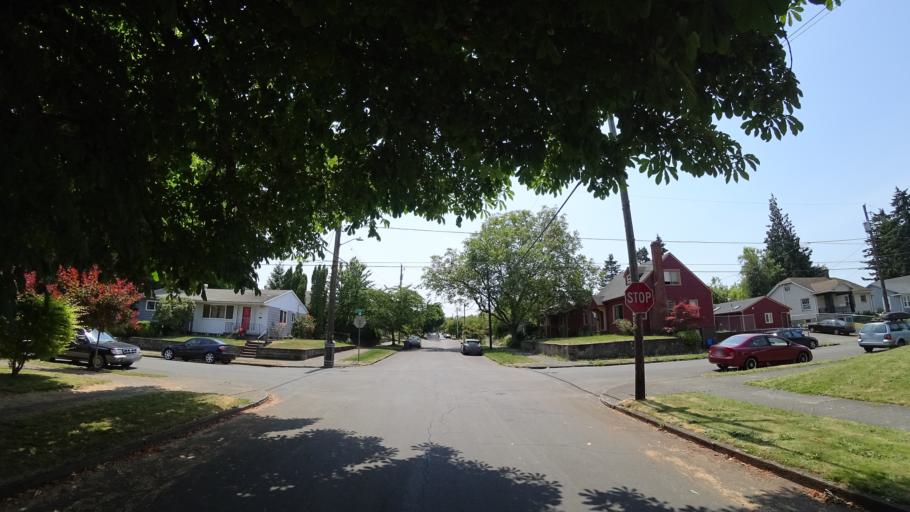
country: US
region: Oregon
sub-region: Multnomah County
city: Portland
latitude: 45.5802
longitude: -122.6763
